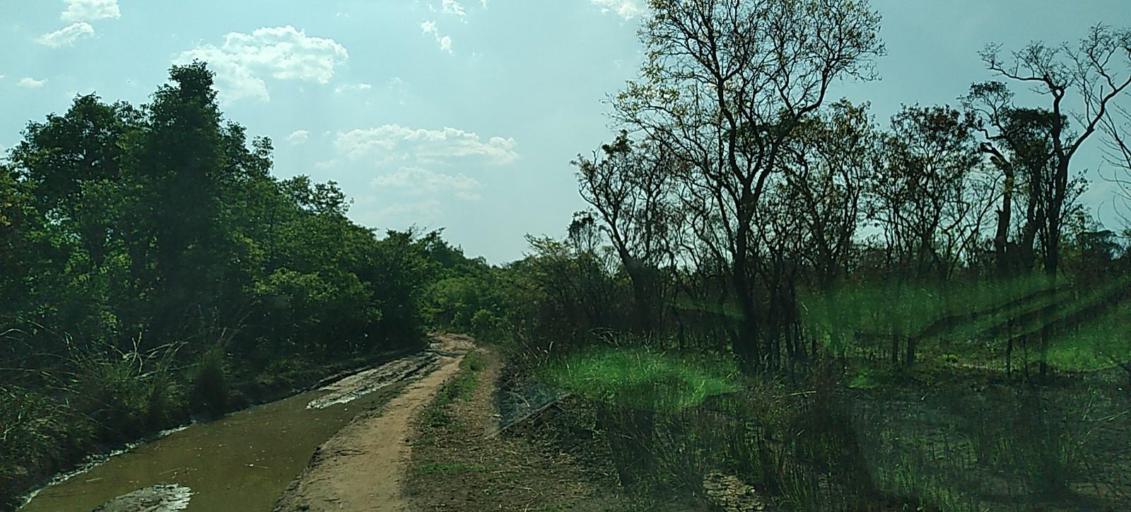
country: ZM
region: North-Western
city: Mwinilunga
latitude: -11.2976
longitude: 24.8606
